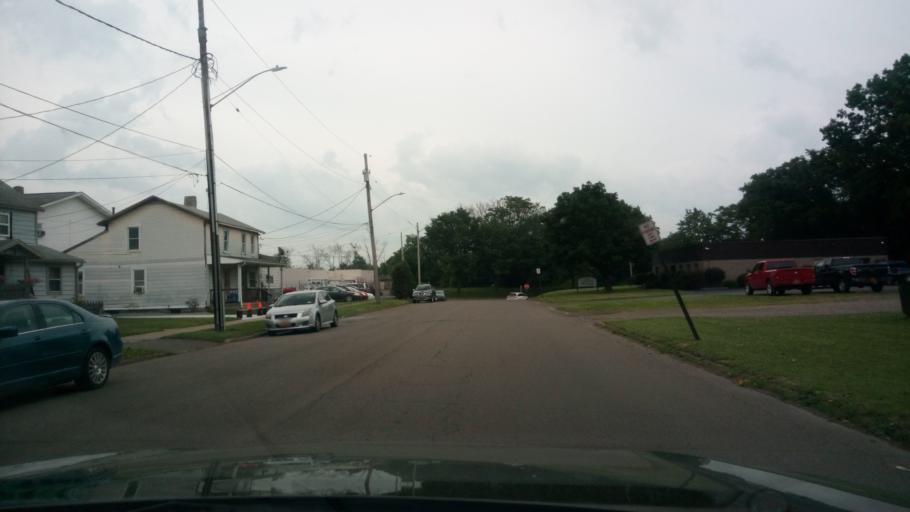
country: US
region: New York
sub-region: Chemung County
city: Elmira
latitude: 42.1022
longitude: -76.8072
